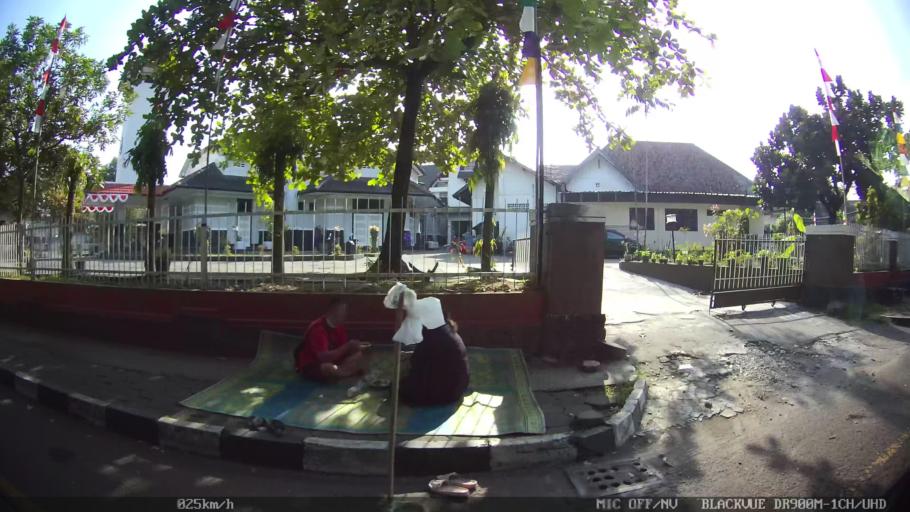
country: ID
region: Daerah Istimewa Yogyakarta
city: Yogyakarta
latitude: -7.7871
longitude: 110.3699
